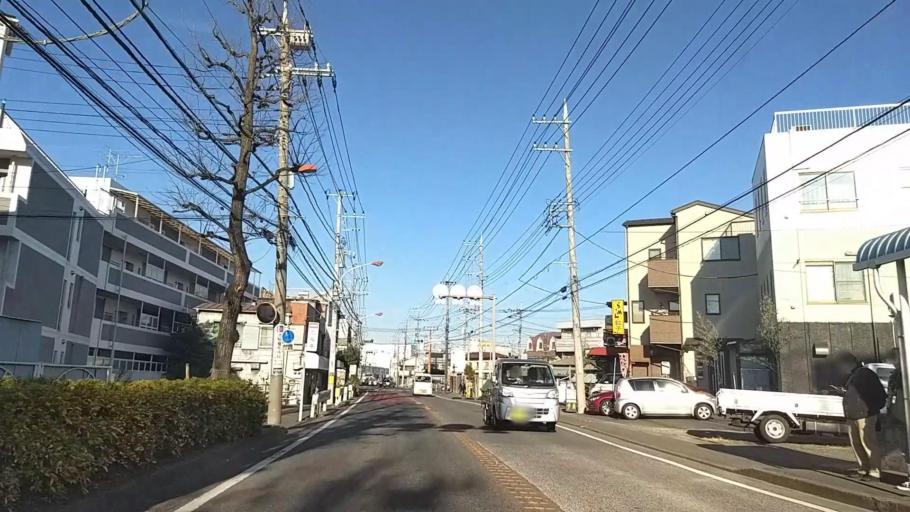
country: JP
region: Kanagawa
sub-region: Kawasaki-shi
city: Kawasaki
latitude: 35.5909
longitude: 139.6379
